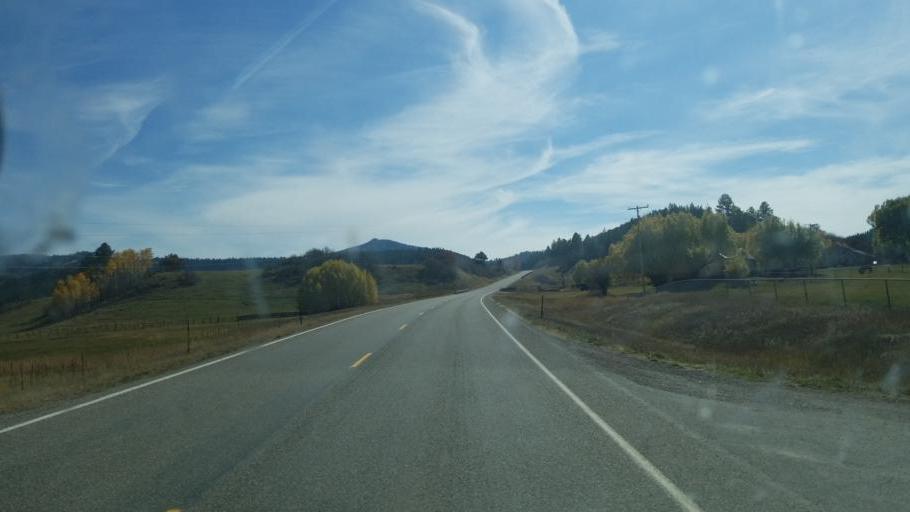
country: US
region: New Mexico
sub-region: Rio Arriba County
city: Dulce
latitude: 37.0028
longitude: -106.7917
